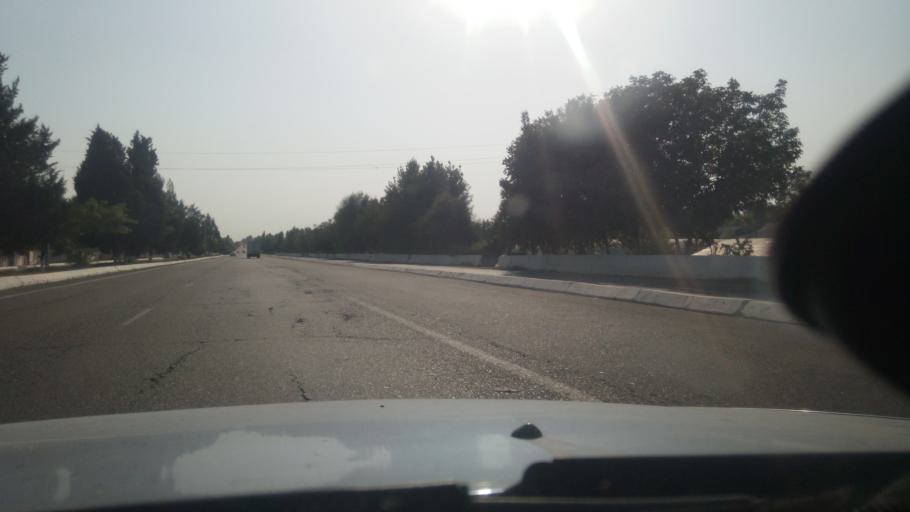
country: UZ
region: Toshkent
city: Zafar
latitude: 41.0110
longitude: 68.8387
